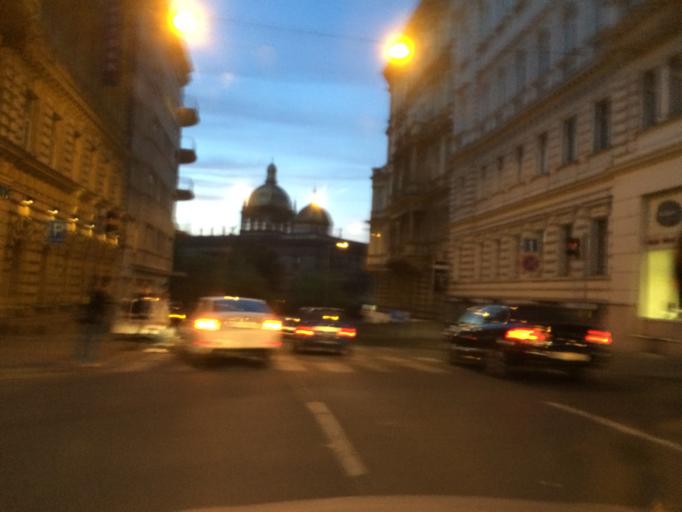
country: CZ
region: Praha
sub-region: Praha 1
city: Stare Mesto
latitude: 50.0771
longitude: 14.4304
